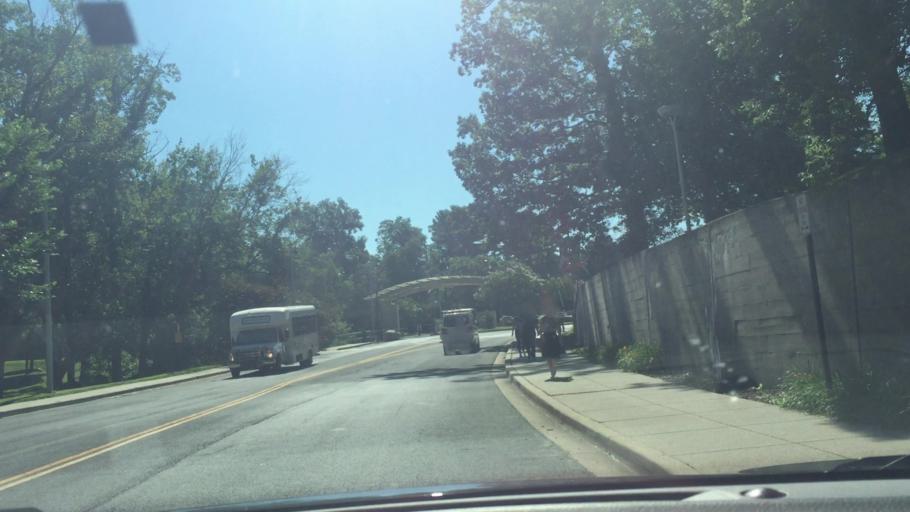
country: US
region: Maryland
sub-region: Montgomery County
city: Bethesda
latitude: 39.0003
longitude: -77.1001
